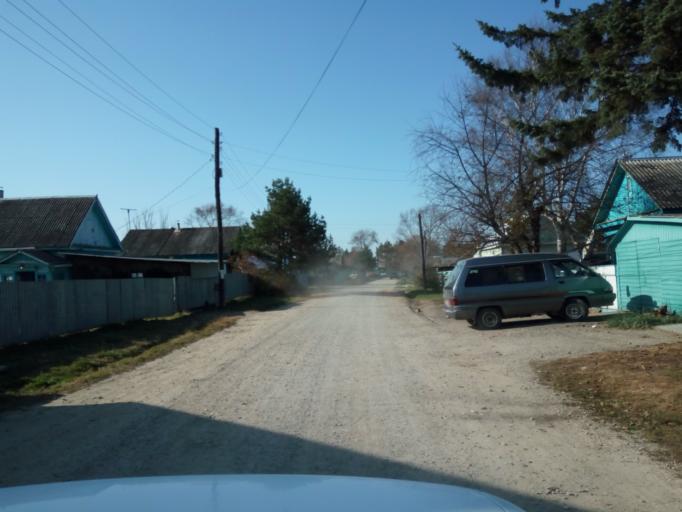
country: RU
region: Primorskiy
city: Dal'nerechensk
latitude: 45.9263
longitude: 133.7188
